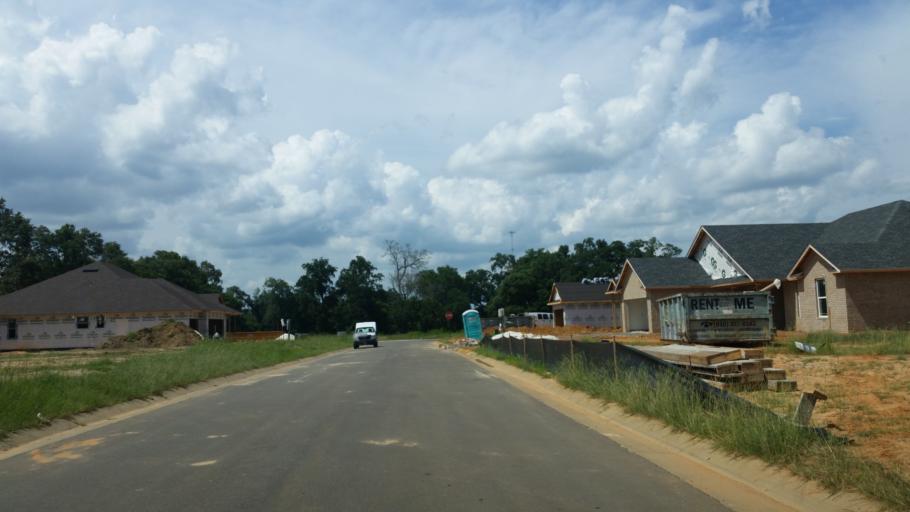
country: US
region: Florida
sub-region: Escambia County
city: Cantonment
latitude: 30.5534
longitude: -87.3700
